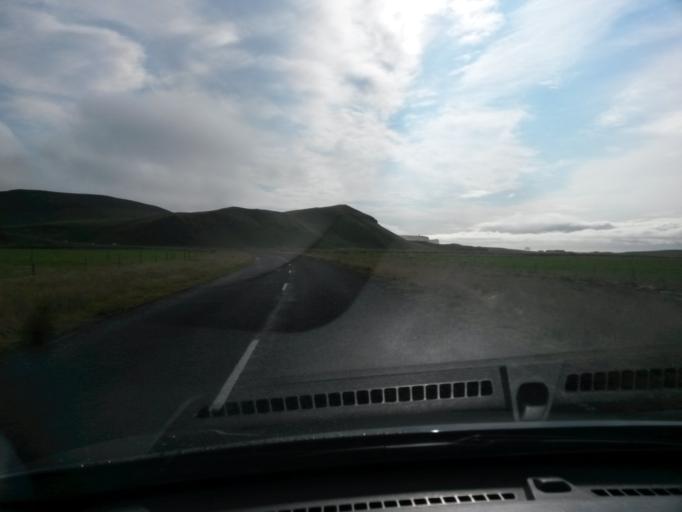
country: IS
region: South
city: Vestmannaeyjar
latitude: 63.4328
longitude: -19.1882
